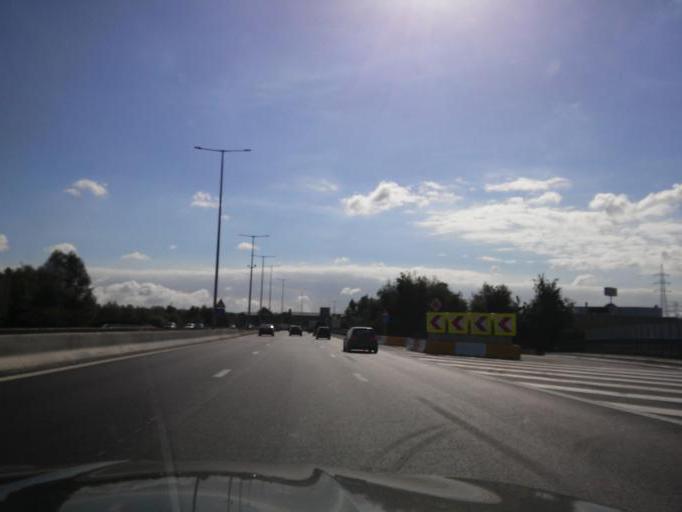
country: BE
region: Flanders
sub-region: Provincie Vlaams-Brabant
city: Drogenbos
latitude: 50.8038
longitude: 4.3052
